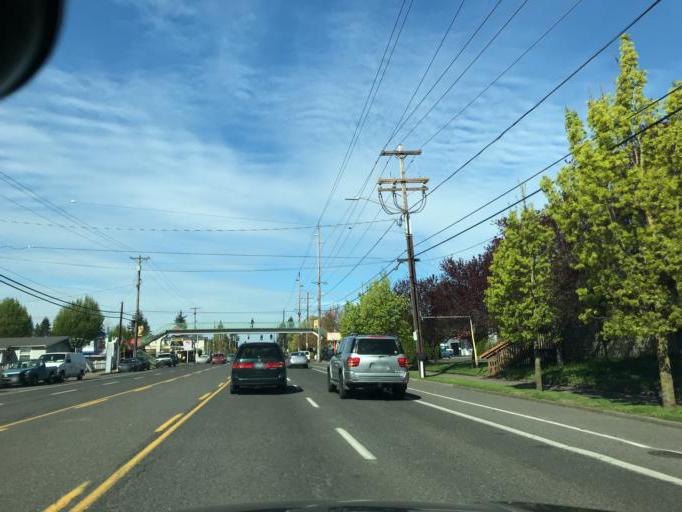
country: US
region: Oregon
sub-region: Multnomah County
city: Lents
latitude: 45.5041
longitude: -122.5217
